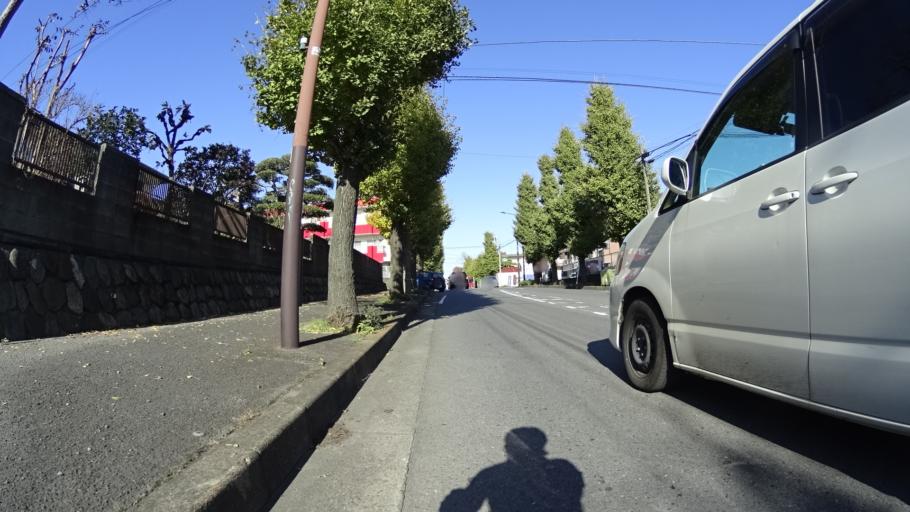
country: JP
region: Tokyo
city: Hachioji
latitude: 35.5754
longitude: 139.3602
